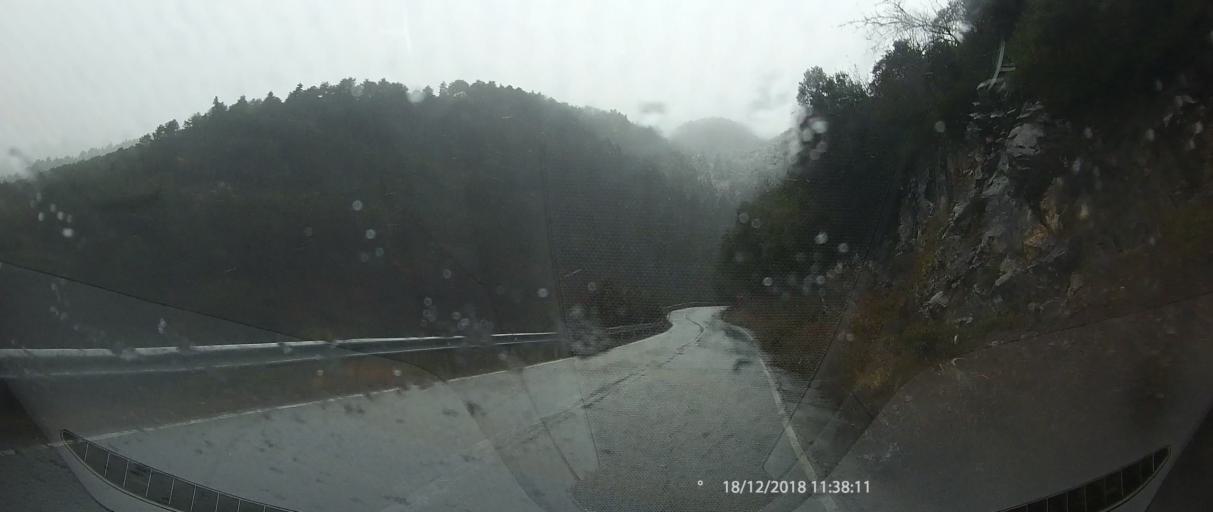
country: GR
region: Central Macedonia
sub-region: Nomos Pierias
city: Litochoro
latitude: 40.1123
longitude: 22.4801
